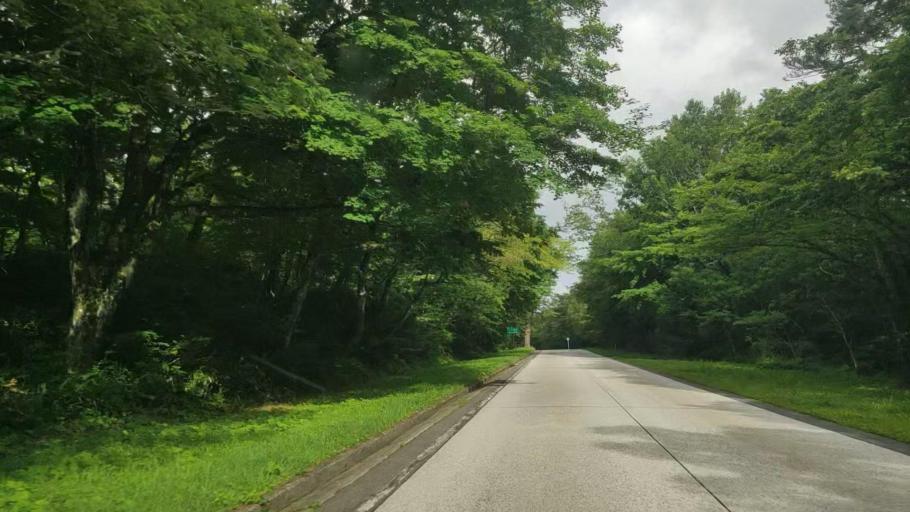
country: JP
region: Tottori
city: Yonago
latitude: 35.3970
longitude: 133.5144
